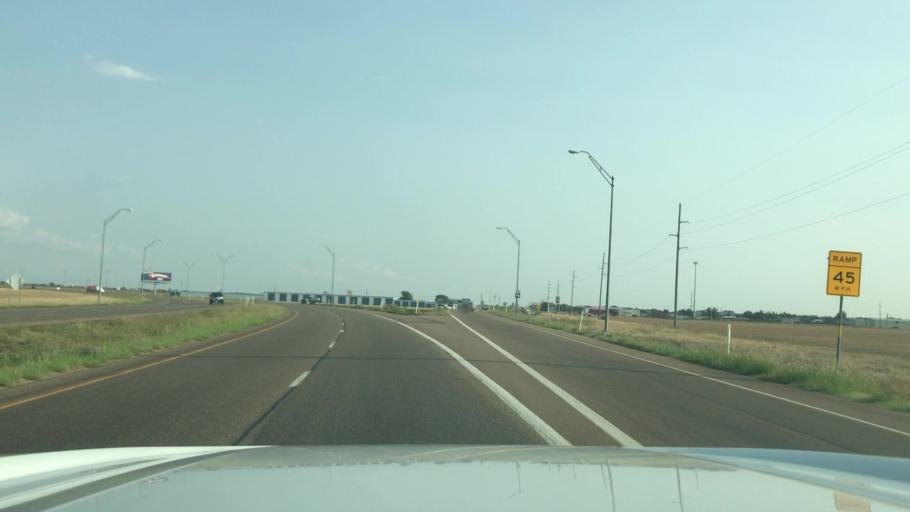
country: US
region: Texas
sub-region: Randall County
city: Canyon
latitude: 35.1226
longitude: -101.9380
